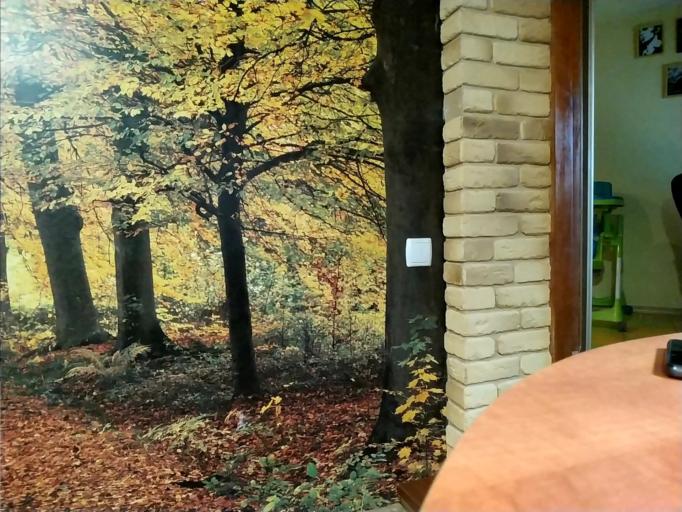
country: BY
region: Minsk
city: Il'ya
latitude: 54.4232
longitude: 27.4956
